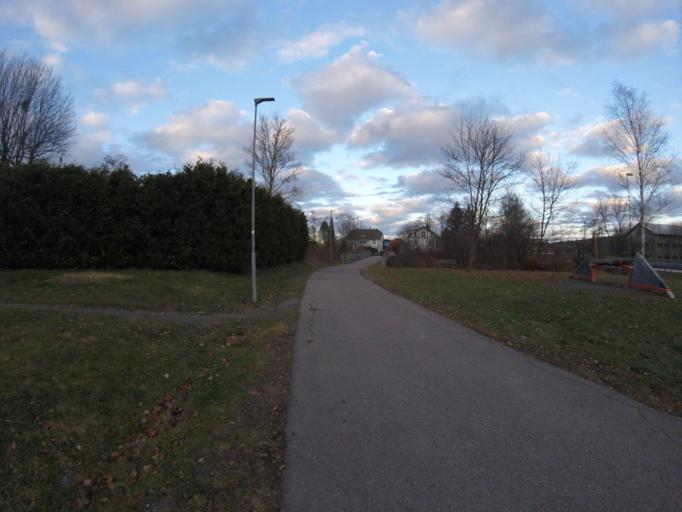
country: NO
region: Akershus
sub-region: Skedsmo
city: Leirsund
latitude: 59.9972
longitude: 11.0877
